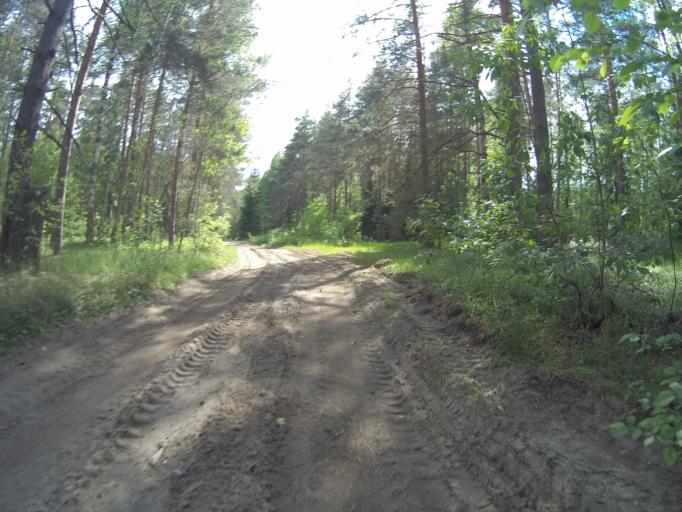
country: RU
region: Vladimir
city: Raduzhnyy
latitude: 55.9800
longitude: 40.2591
